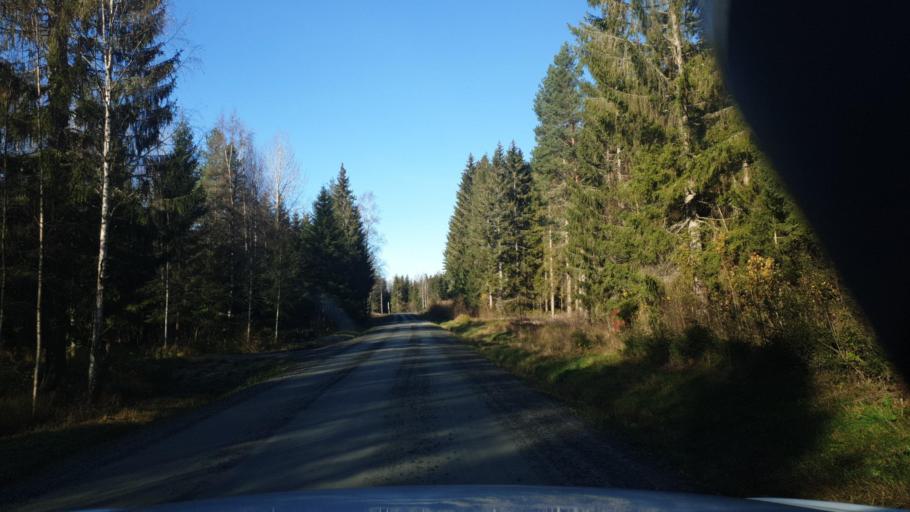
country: SE
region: Vaermland
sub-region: Karlstads Kommun
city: Edsvalla
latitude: 59.4470
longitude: 13.1583
